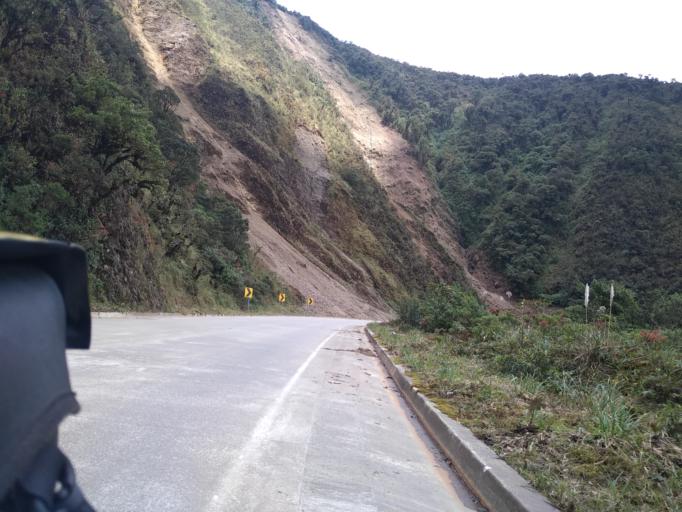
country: EC
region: Zamora-Chinchipe
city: Zamora
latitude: -4.4364
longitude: -79.1468
